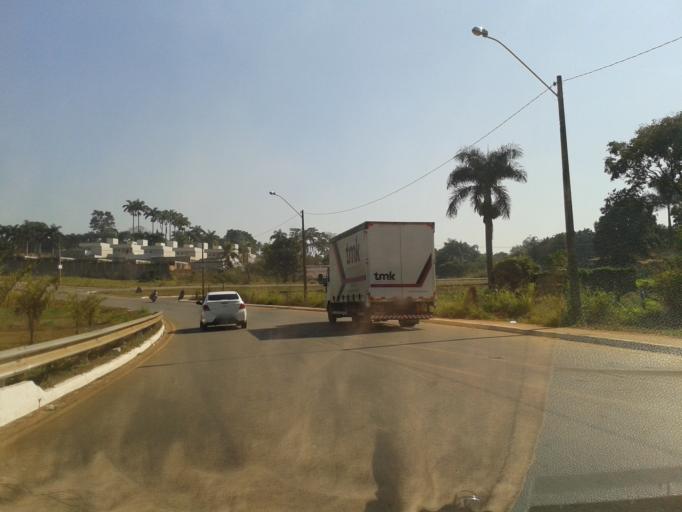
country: BR
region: Goias
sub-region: Aparecida De Goiania
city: Aparecida de Goiania
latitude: -16.7669
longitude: -49.3015
